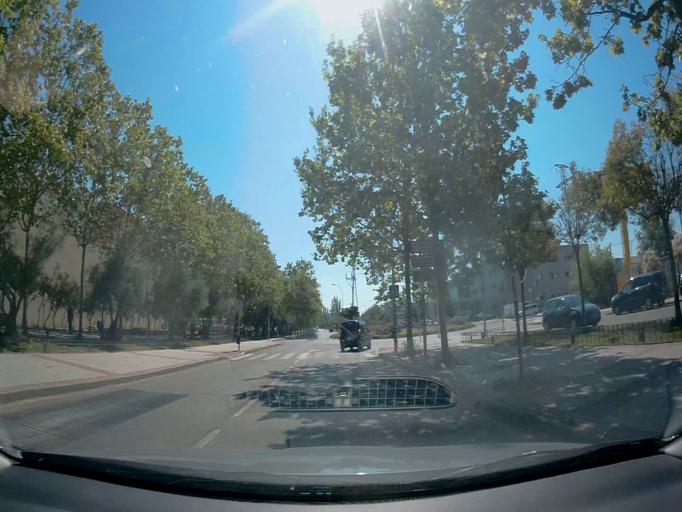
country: ES
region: Madrid
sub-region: Provincia de Madrid
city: Alcorcon
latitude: 40.3444
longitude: -3.8101
